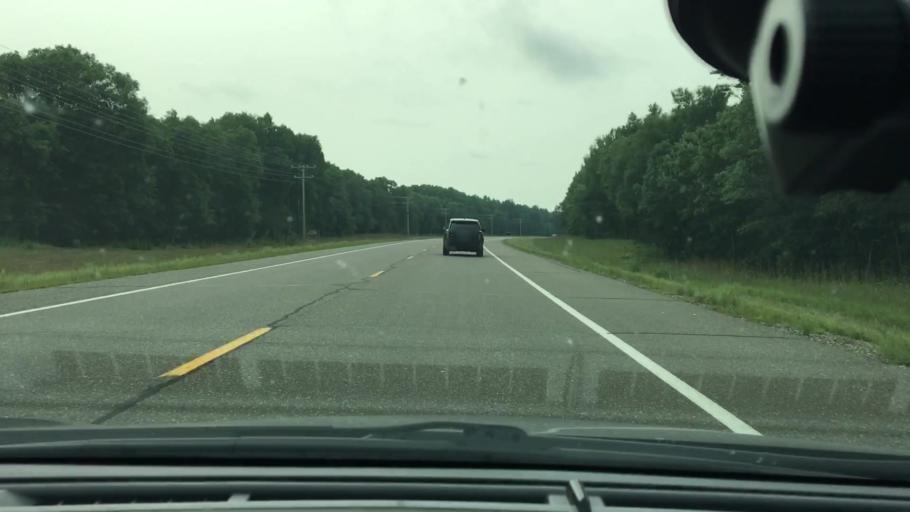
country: US
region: Minnesota
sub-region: Crow Wing County
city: Cross Lake
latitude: 46.6053
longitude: -94.1310
